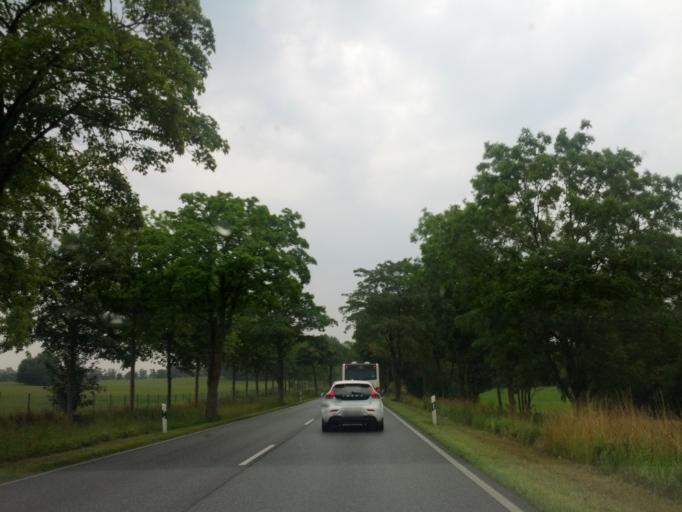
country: DE
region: Mecklenburg-Vorpommern
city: Lambrechtshagen
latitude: 54.1106
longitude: 12.0031
